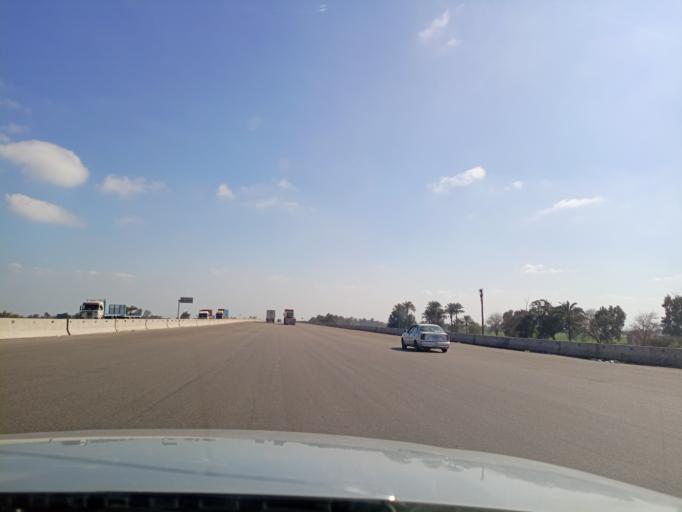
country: EG
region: Muhafazat al Qalyubiyah
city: Banha
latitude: 30.4651
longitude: 31.3034
